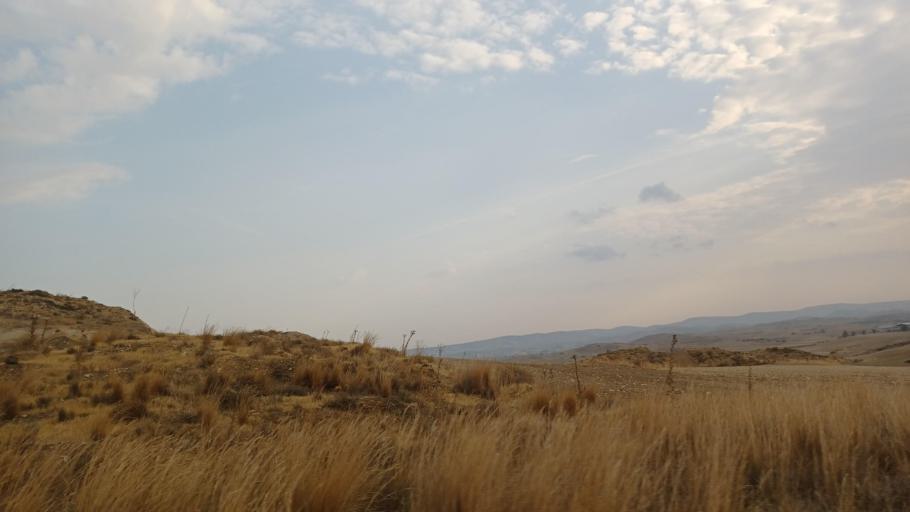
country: CY
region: Larnaka
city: Troulloi
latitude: 35.0207
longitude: 33.5736
